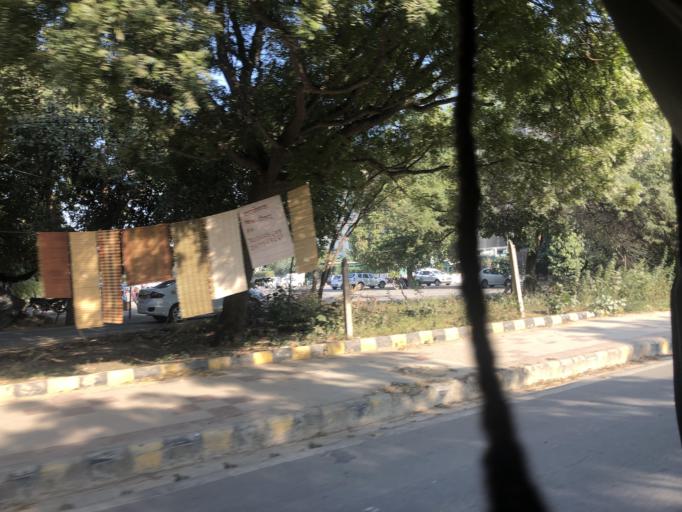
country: IN
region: Haryana
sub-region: Gurgaon
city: Gurgaon
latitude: 28.4621
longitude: 77.0665
